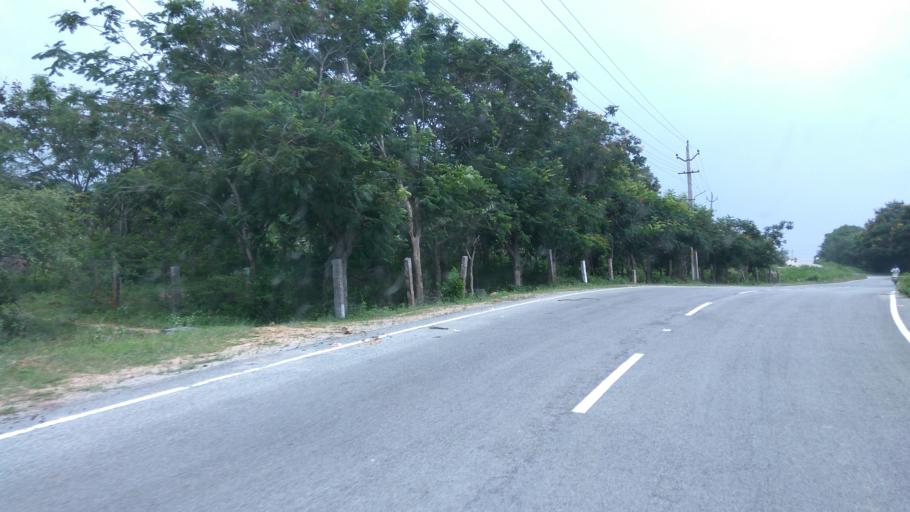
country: IN
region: Telangana
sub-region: Rangareddi
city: Ghatkesar
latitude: 17.5386
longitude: 78.6916
